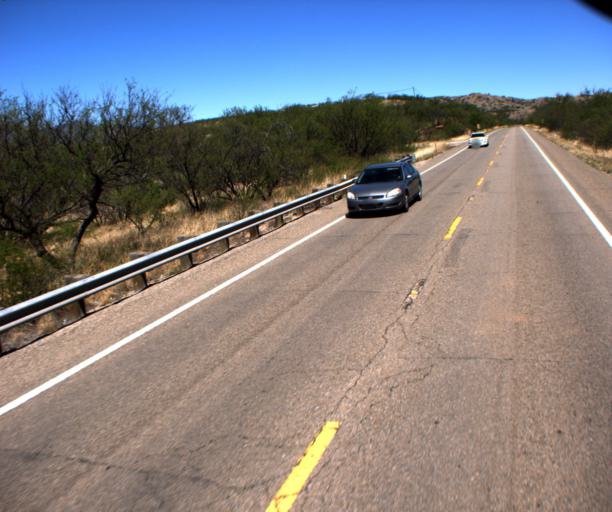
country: US
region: Arizona
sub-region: Santa Cruz County
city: Rio Rico
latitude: 31.6431
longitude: -110.7146
